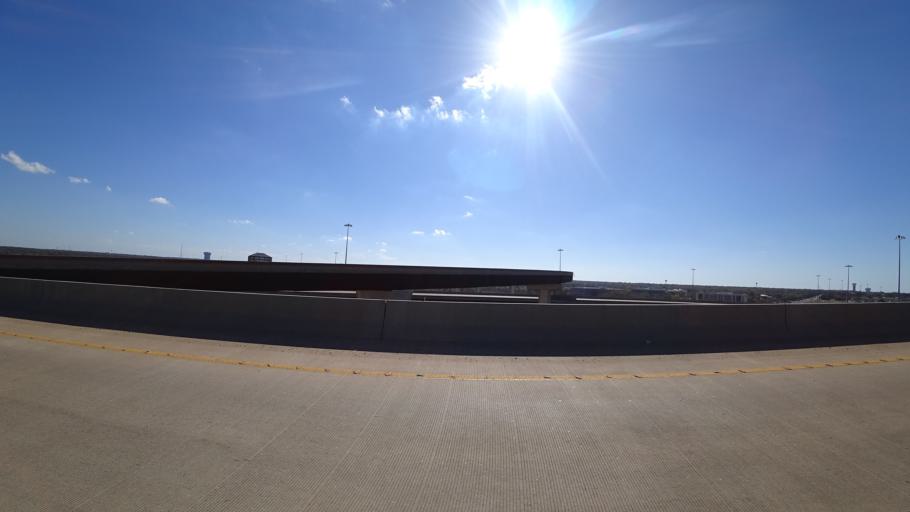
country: US
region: Texas
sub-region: Williamson County
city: Anderson Mill
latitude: 30.4695
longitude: -97.7959
